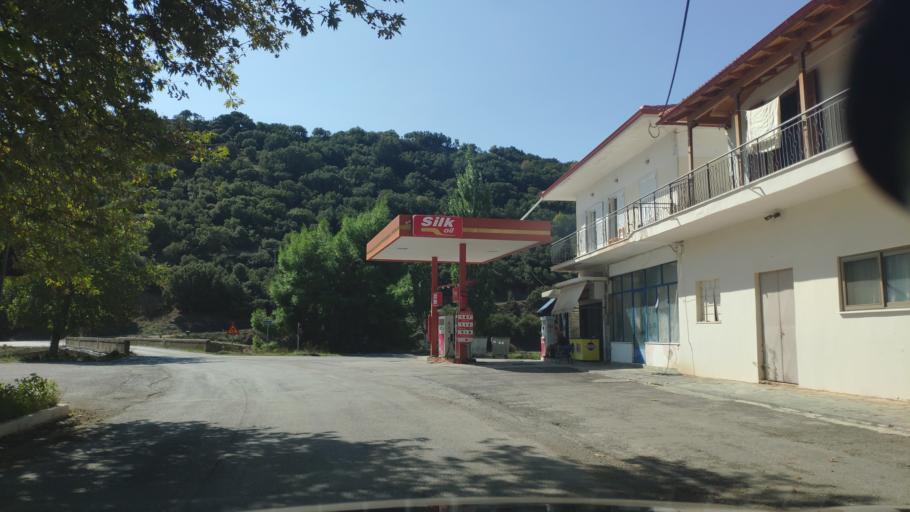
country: GR
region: Peloponnese
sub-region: Nomos Korinthias
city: Nemea
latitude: 37.8878
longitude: 22.4973
